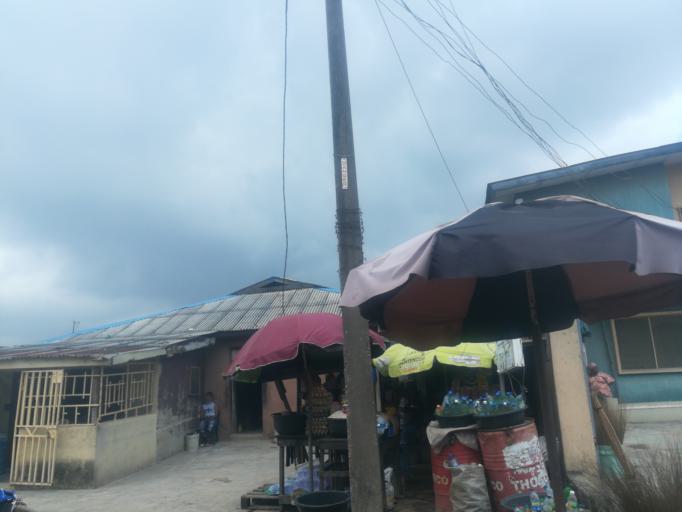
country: NG
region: Lagos
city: Somolu
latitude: 6.5527
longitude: 3.3941
